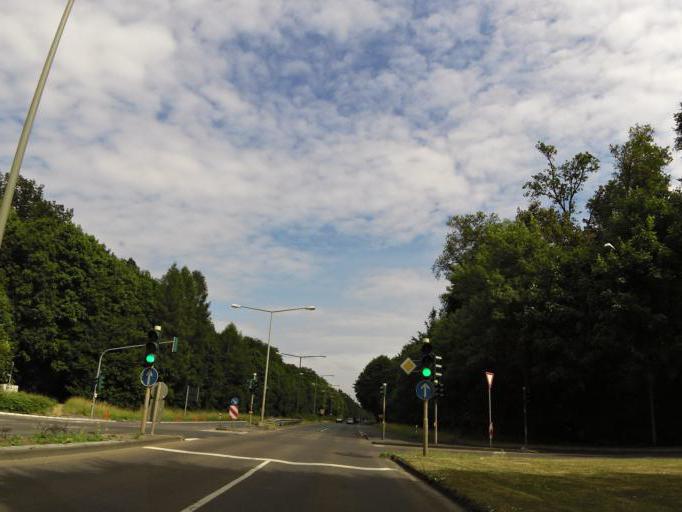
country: DE
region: Hesse
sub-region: Regierungsbezirk Darmstadt
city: Frankfurt am Main
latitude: 50.0845
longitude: 8.6990
